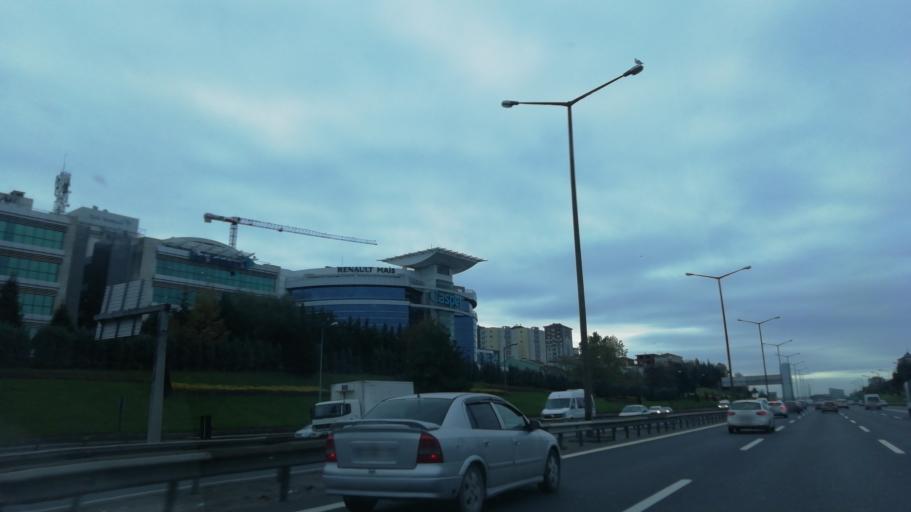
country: TR
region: Istanbul
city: Umraniye
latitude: 41.0275
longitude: 29.1208
